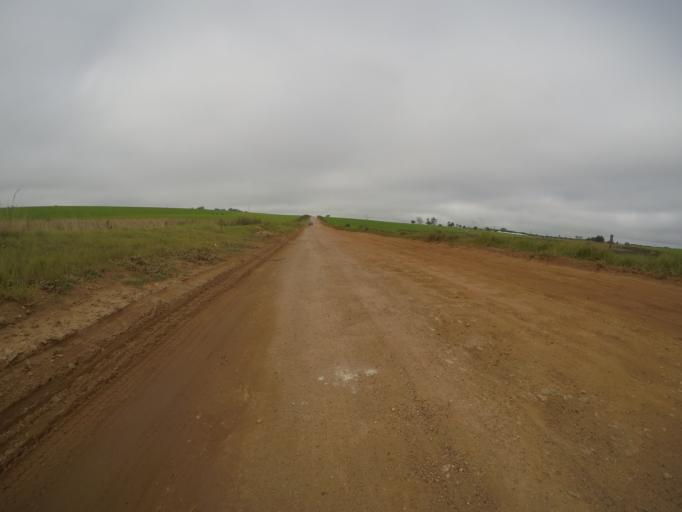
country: ZA
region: Eastern Cape
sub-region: Cacadu District Municipality
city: Kareedouw
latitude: -34.0271
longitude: 24.2424
